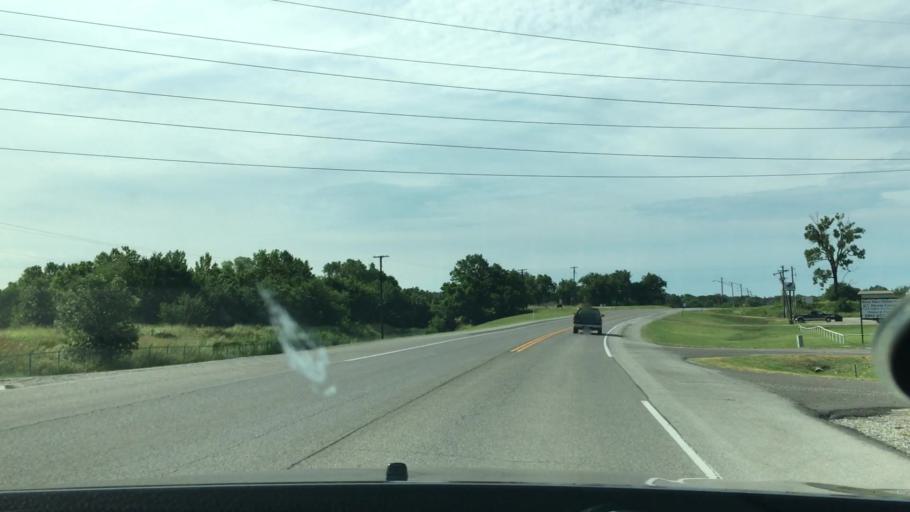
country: US
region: Oklahoma
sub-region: Murray County
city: Sulphur
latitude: 34.5229
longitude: -96.9693
